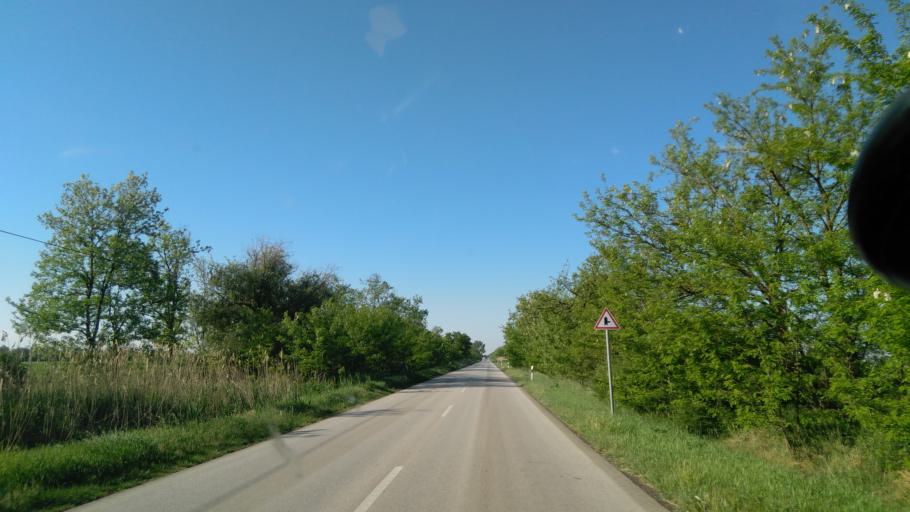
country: HU
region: Bekes
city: Elek
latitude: 46.5554
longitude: 21.2609
